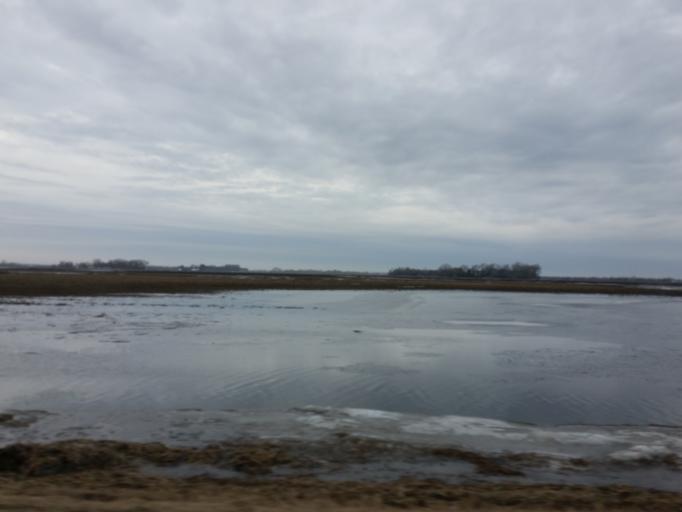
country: US
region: North Dakota
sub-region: Walsh County
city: Grafton
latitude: 48.3883
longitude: -97.4703
